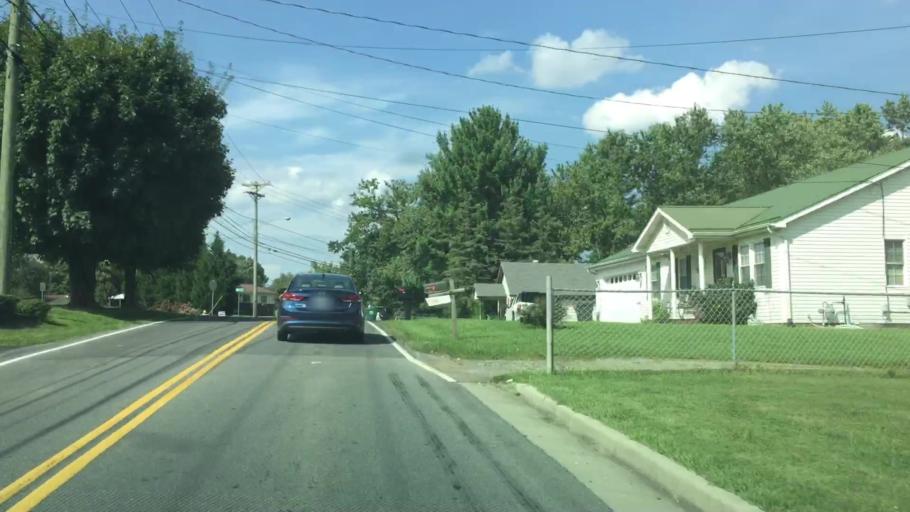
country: US
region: Tennessee
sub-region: Sullivan County
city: Fairmount
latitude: 36.6120
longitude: -82.1383
